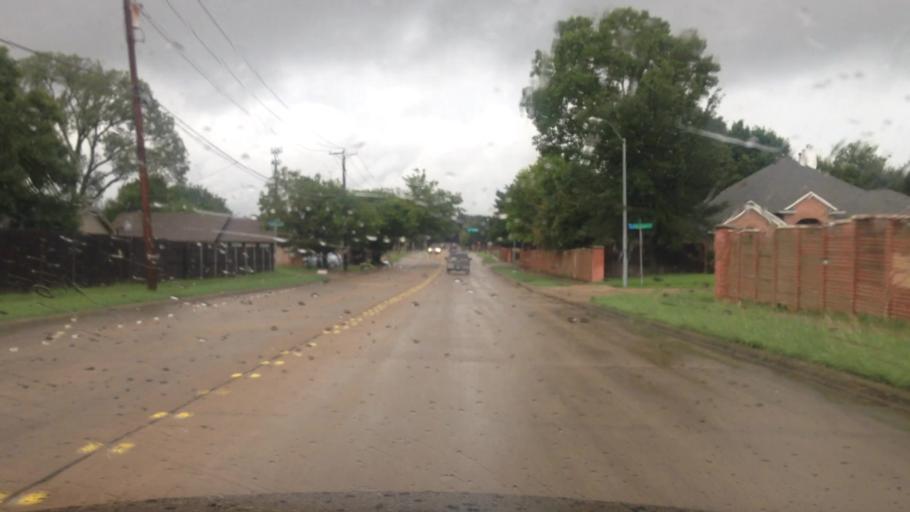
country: US
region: Texas
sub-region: Tarrant County
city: Watauga
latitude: 32.8821
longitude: -97.2145
